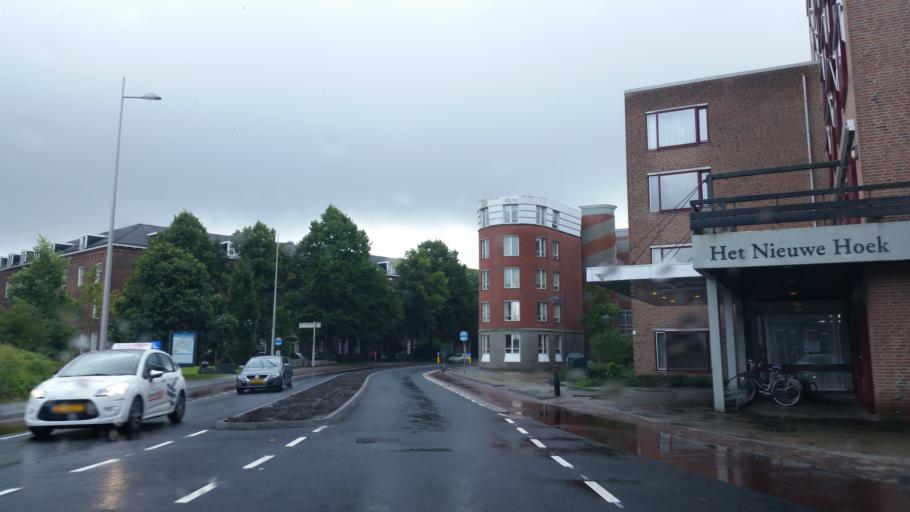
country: NL
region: Friesland
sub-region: Gemeente Leeuwarden
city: Leeuwarden
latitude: 53.2054
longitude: 5.8025
